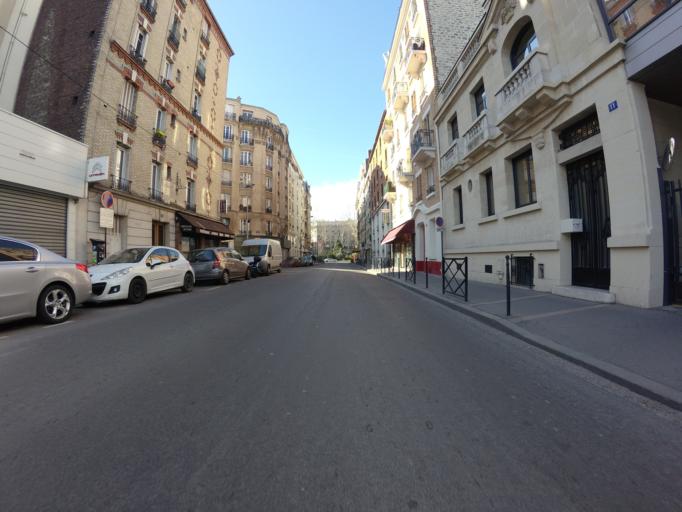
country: FR
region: Ile-de-France
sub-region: Departement des Hauts-de-Seine
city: Clichy
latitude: 48.9033
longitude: 2.3145
